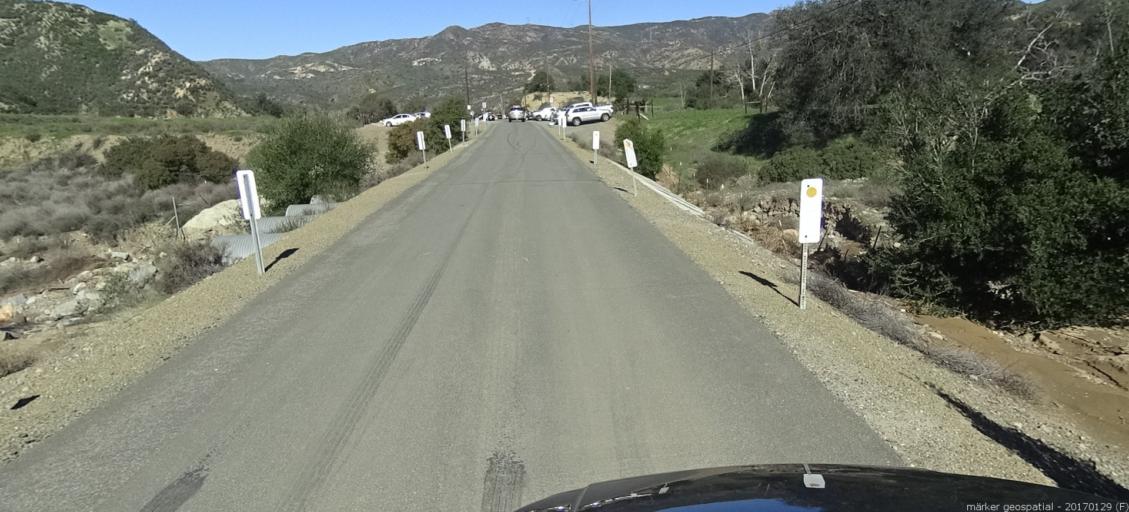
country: US
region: California
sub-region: Orange County
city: Foothill Ranch
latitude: 33.7619
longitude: -117.6773
